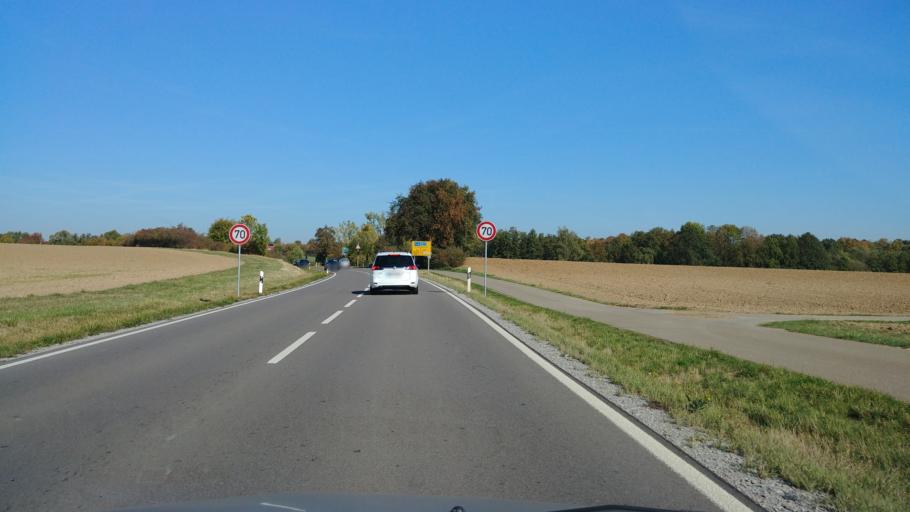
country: DE
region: Baden-Wuerttemberg
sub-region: Regierungsbezirk Stuttgart
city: Schwaebisch Hall
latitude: 49.0942
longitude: 9.7188
